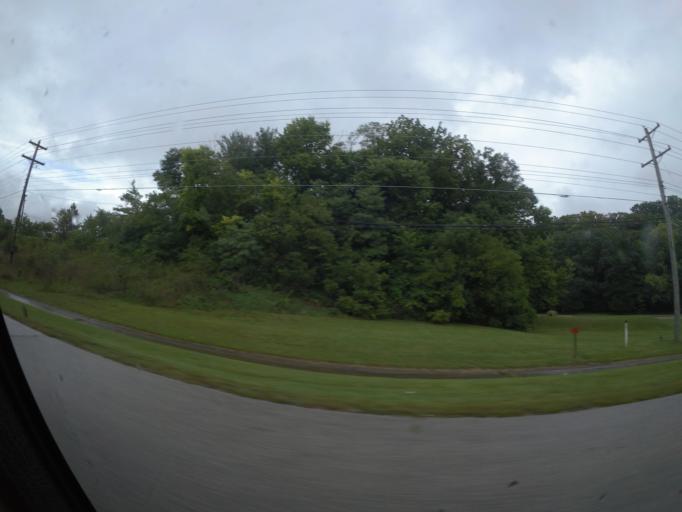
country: US
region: Indiana
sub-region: Montgomery County
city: Crawfordsville
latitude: 40.0578
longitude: -86.9083
